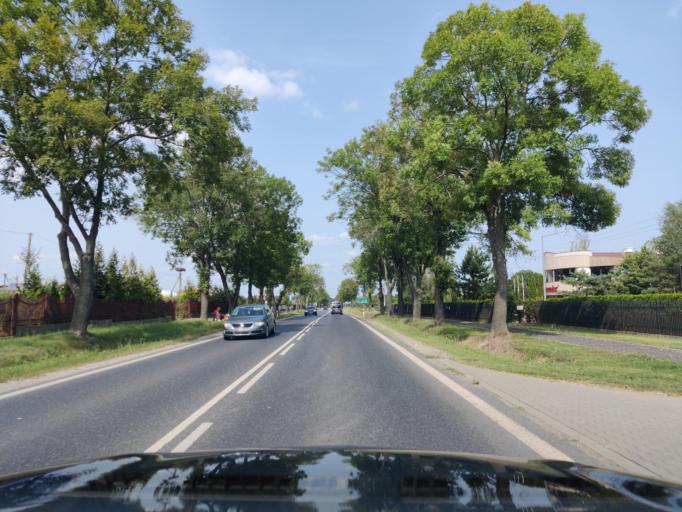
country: PL
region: Masovian Voivodeship
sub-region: Powiat pultuski
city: Pultusk
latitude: 52.7296
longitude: 21.0904
